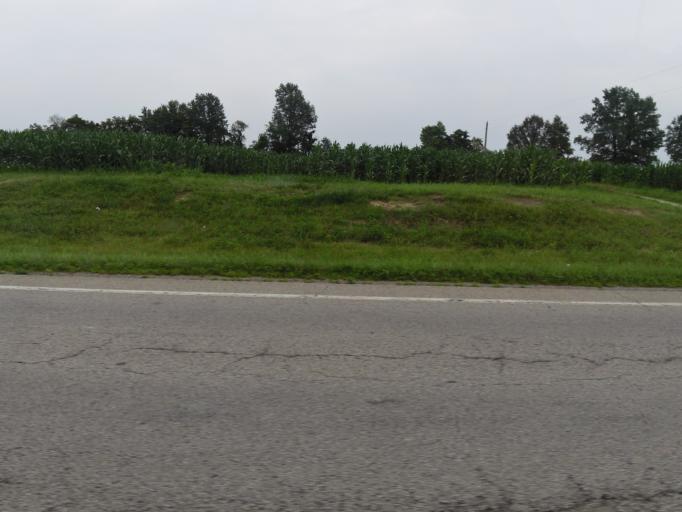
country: US
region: Ohio
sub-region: Clinton County
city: Blanchester
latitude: 39.1676
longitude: -83.9326
